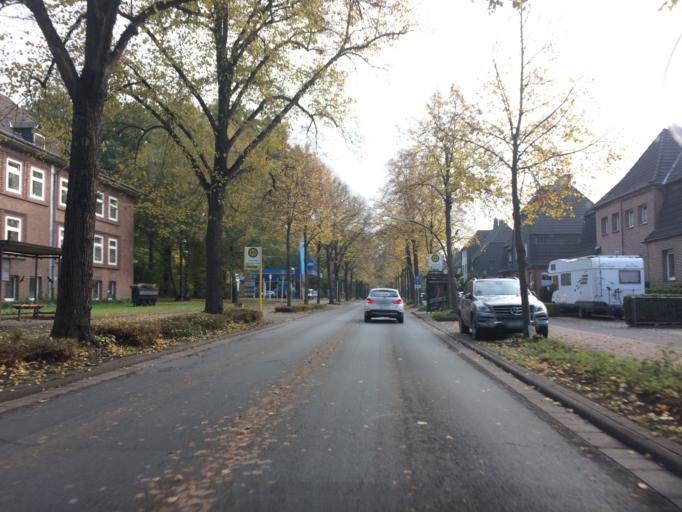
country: DE
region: North Rhine-Westphalia
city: Marl
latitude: 51.6644
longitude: 7.0796
